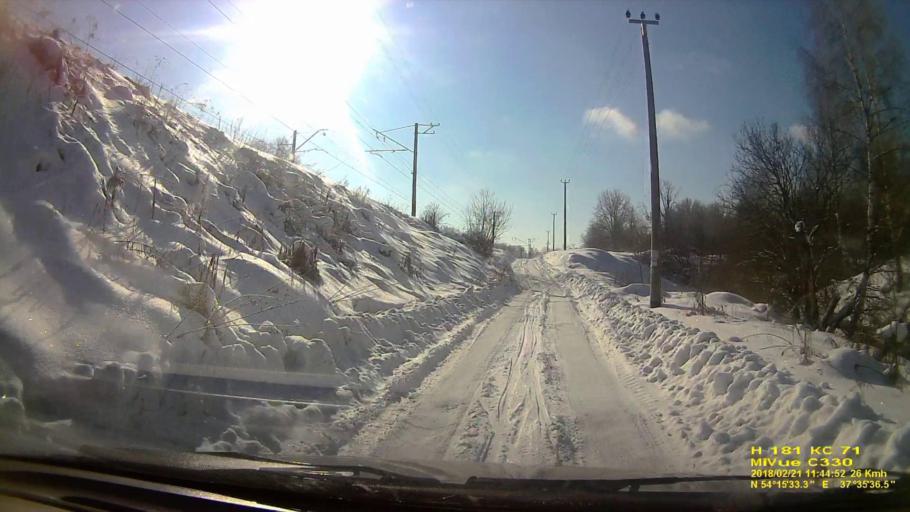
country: RU
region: Tula
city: Gorelki
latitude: 54.2592
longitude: 37.5934
